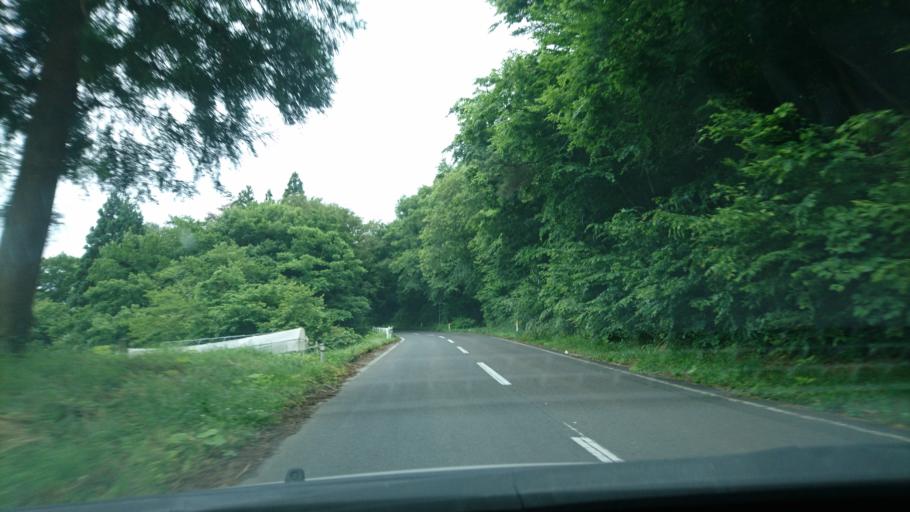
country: JP
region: Iwate
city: Ichinoseki
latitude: 38.9460
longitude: 141.2808
